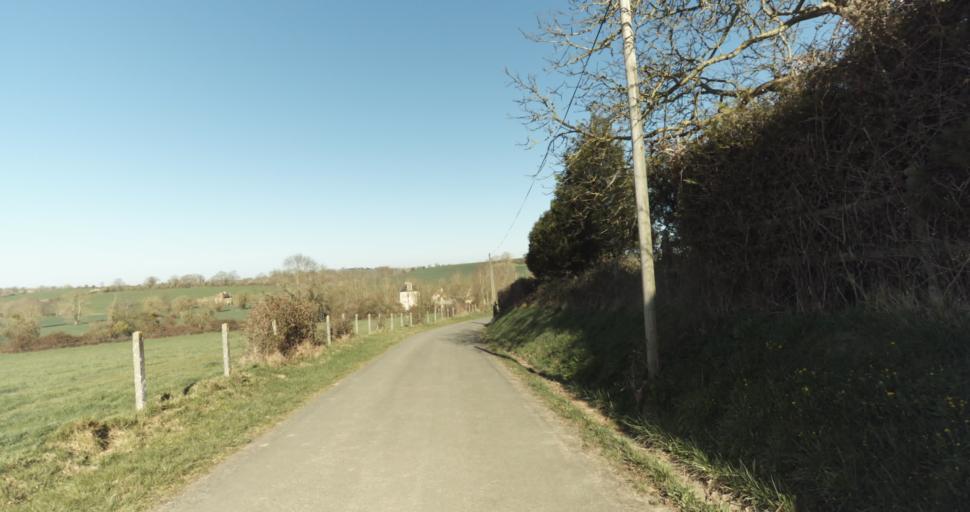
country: FR
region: Lower Normandy
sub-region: Departement du Calvados
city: Saint-Pierre-sur-Dives
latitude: 48.9425
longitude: 0.0319
